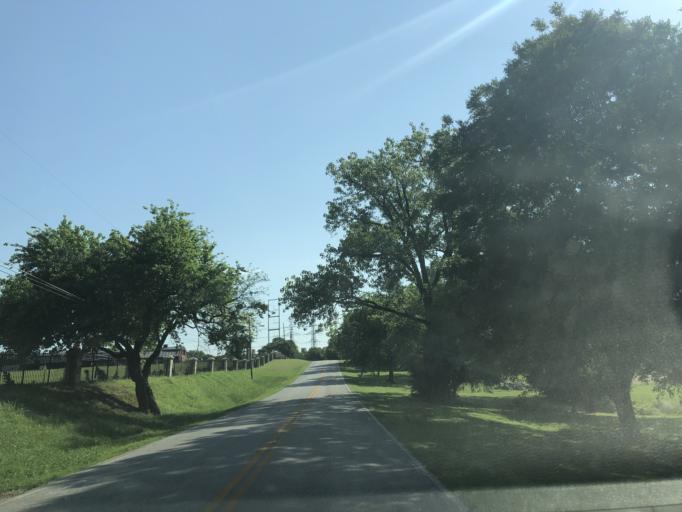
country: US
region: Texas
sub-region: Dallas County
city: Sunnyvale
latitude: 32.8316
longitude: -96.5627
